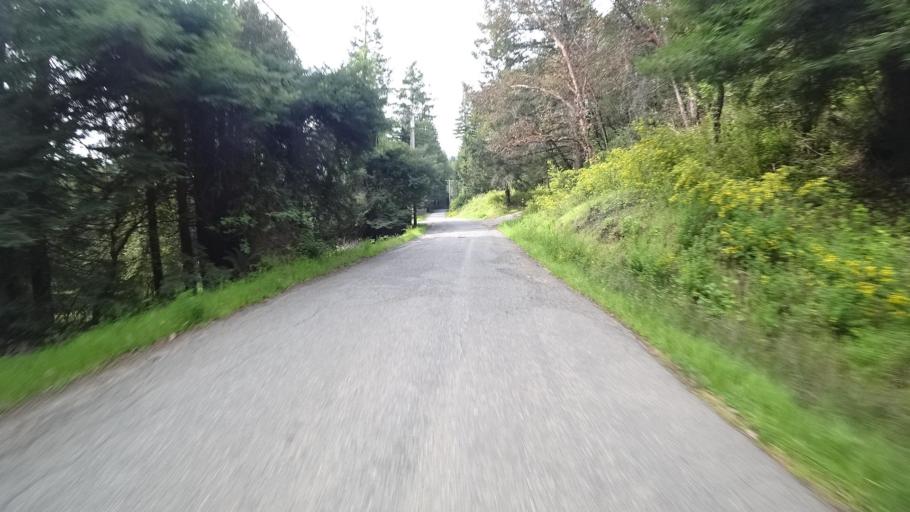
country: US
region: California
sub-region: Humboldt County
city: Redway
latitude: 40.2475
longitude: -123.8328
